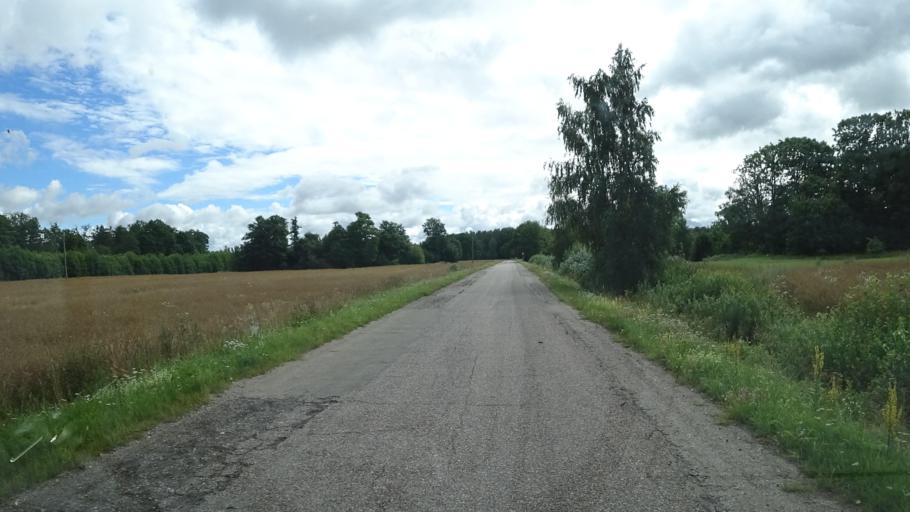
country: LV
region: Liepaja
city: Vec-Liepaja
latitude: 56.6584
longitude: 21.0863
